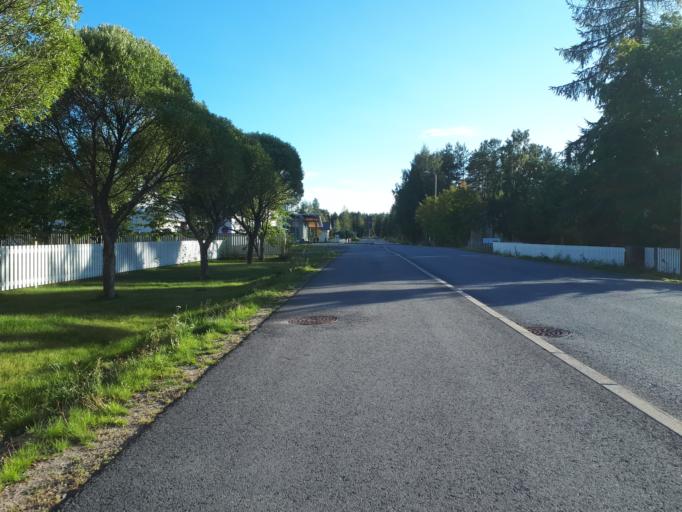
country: FI
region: Northern Ostrobothnia
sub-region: Oulunkaari
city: Ii
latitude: 65.3153
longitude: 25.3866
